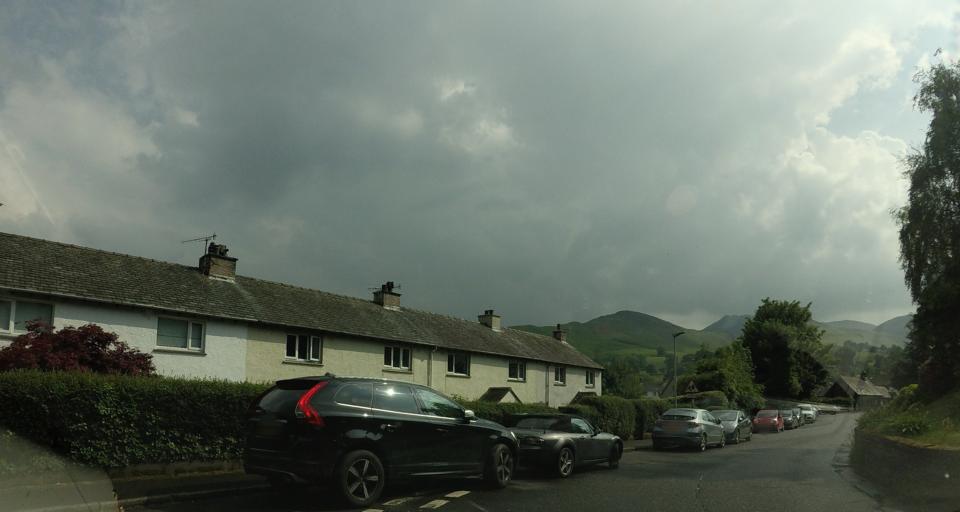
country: GB
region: England
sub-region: Cumbria
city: Keswick
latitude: 54.6036
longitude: -3.1891
